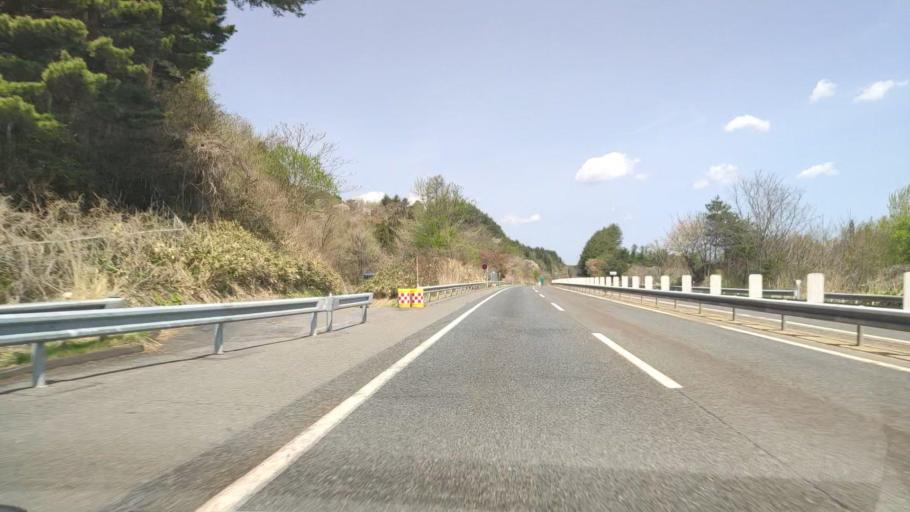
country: JP
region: Iwate
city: Ichinohe
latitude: 40.2643
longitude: 141.3999
